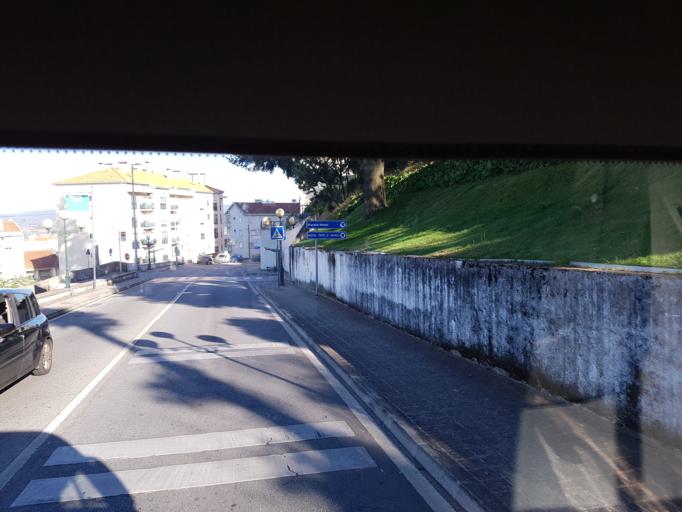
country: PT
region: Castelo Branco
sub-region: Covilha
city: Covilha
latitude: 40.2747
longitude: -7.5038
